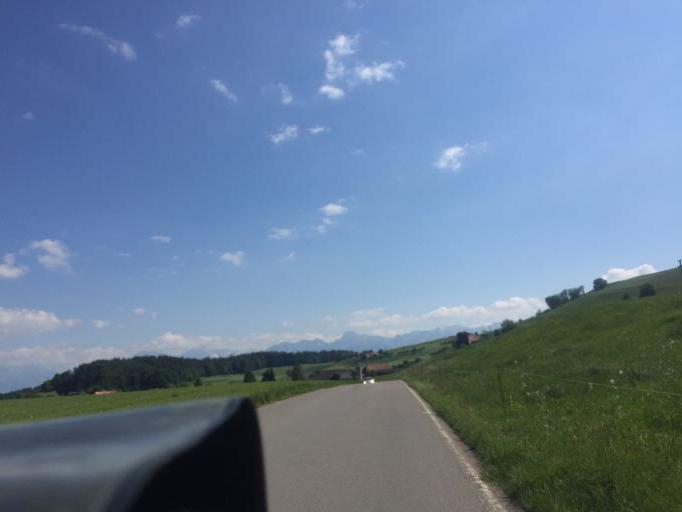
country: CH
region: Bern
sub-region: Bern-Mittelland District
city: Munsingen
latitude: 46.8665
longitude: 7.5316
